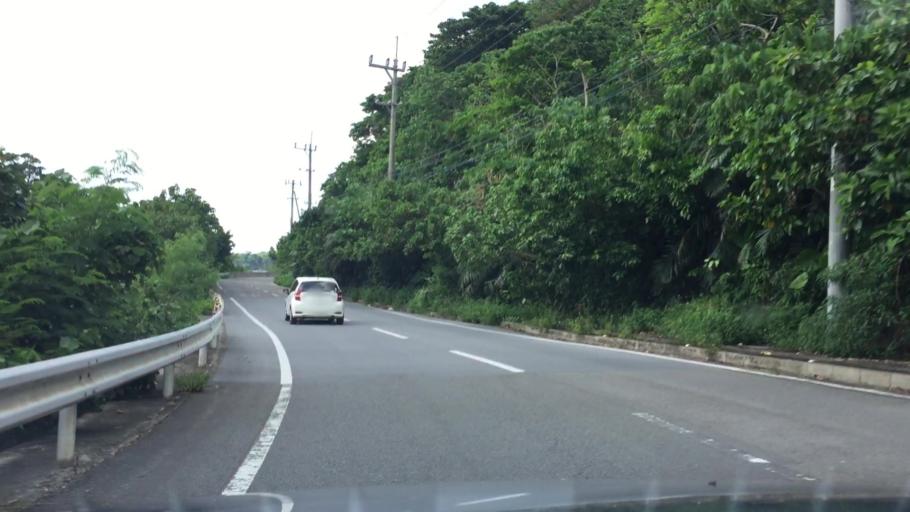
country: JP
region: Okinawa
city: Ishigaki
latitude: 24.4602
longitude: 124.2266
